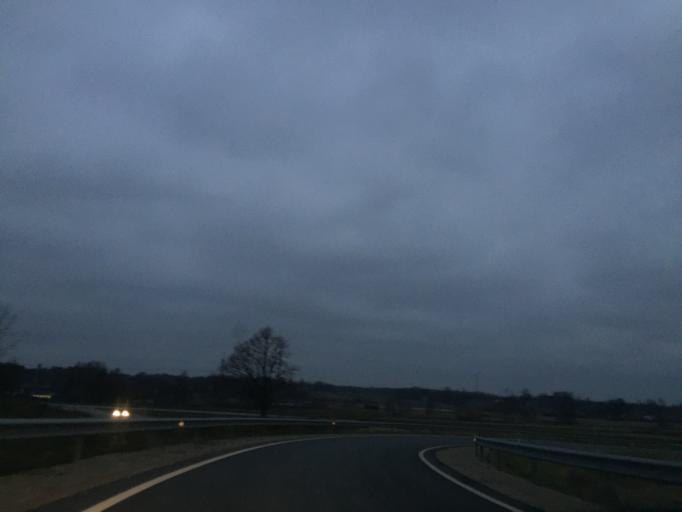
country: LV
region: Koceni
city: Koceni
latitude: 57.5218
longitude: 25.3724
